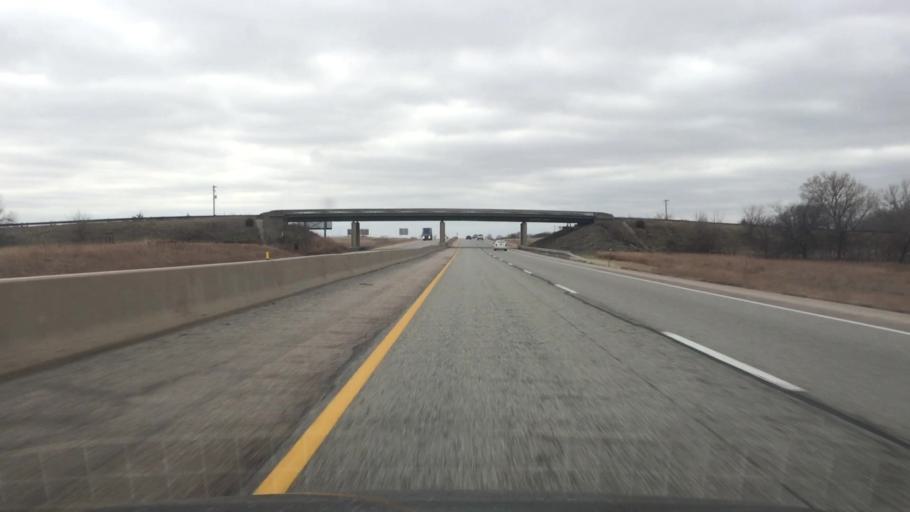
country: US
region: Kansas
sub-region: Butler County
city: El Dorado
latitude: 38.0296
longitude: -96.6589
